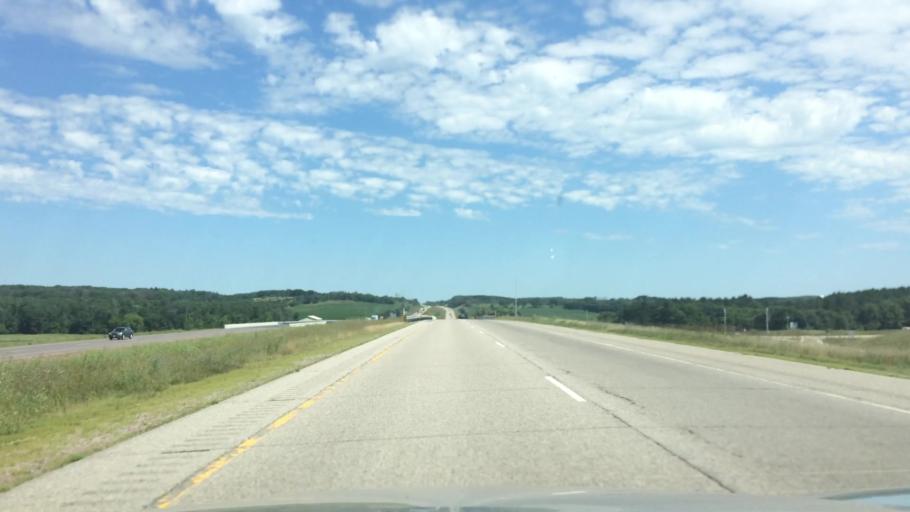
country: US
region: Wisconsin
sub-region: Marquette County
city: Westfield
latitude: 43.7886
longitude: -89.4833
